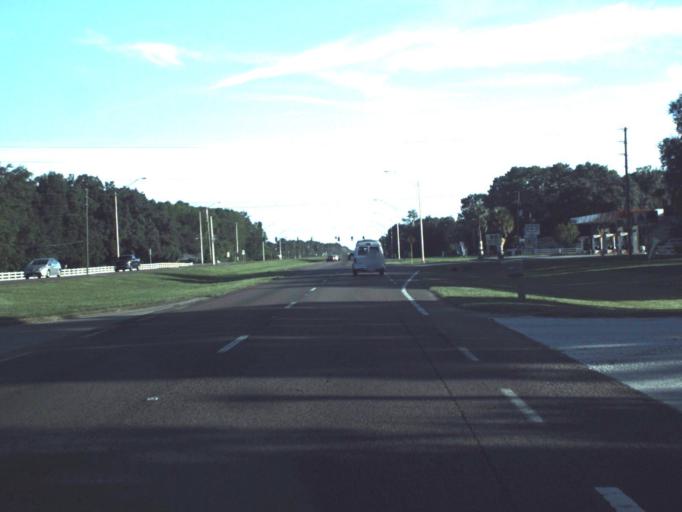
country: US
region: Florida
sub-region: Citrus County
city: Sugarmill Woods
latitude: 28.7459
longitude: -82.5531
